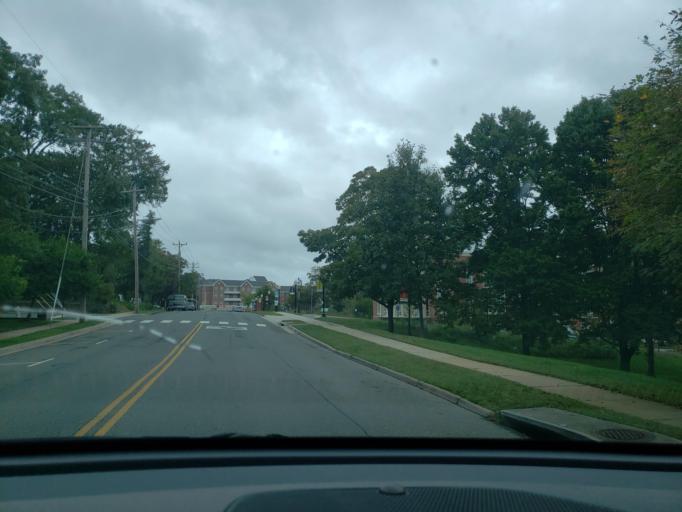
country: US
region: Virginia
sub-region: City of Fredericksburg
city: Fredericksburg
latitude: 38.3050
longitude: -77.4785
